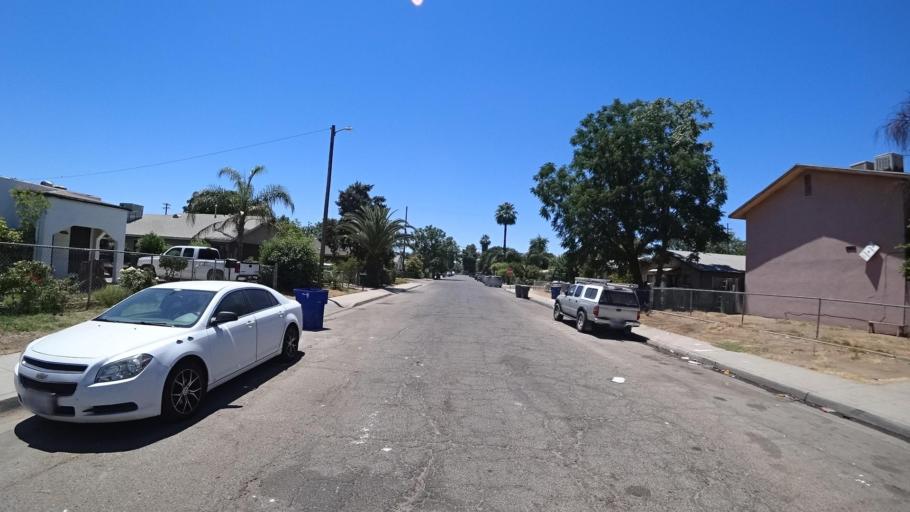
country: US
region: California
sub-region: Fresno County
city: Fresno
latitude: 36.7127
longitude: -119.7559
